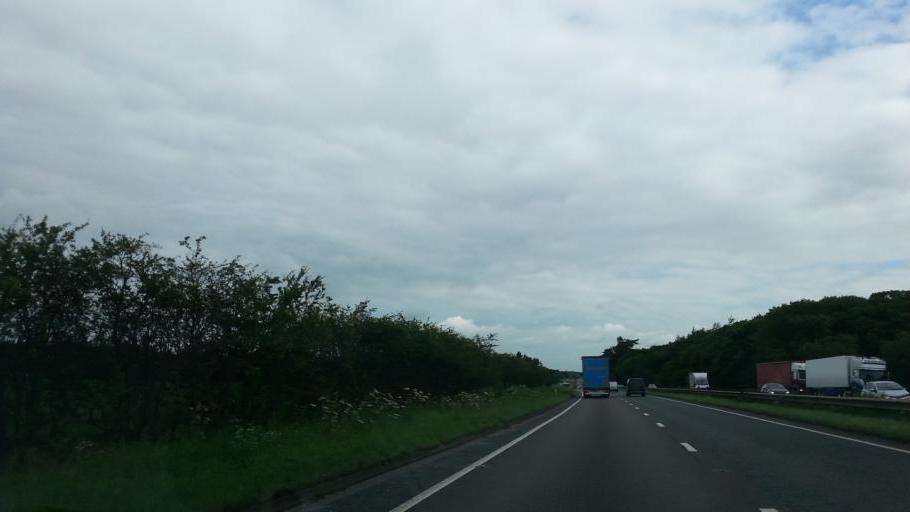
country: GB
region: England
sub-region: Nottinghamshire
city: Babworth
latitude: 53.3067
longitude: -1.0306
